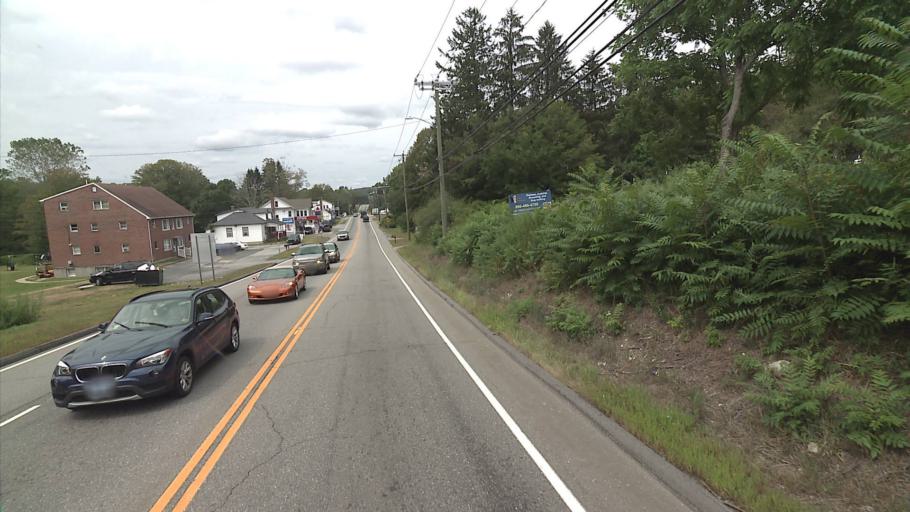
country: US
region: Connecticut
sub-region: New London County
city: Montville Center
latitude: 41.4280
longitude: -72.2155
